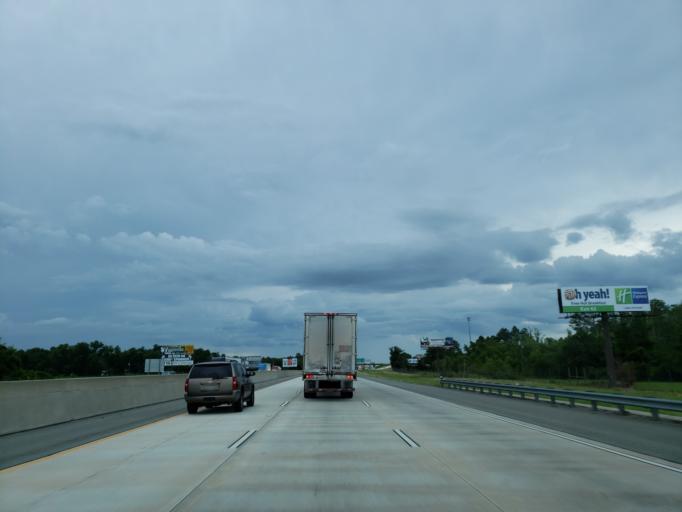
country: US
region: Georgia
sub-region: Cook County
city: Sparks
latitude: 31.1589
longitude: -83.4472
